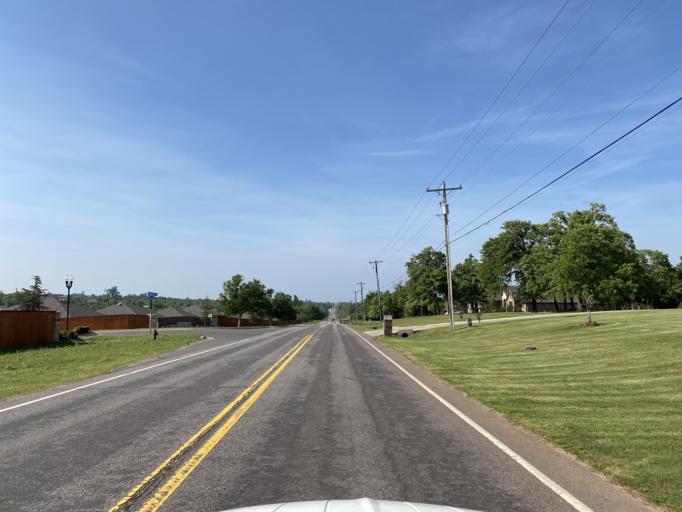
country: US
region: Oklahoma
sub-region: Oklahoma County
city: Nicoma Park
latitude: 35.4378
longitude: -97.3357
